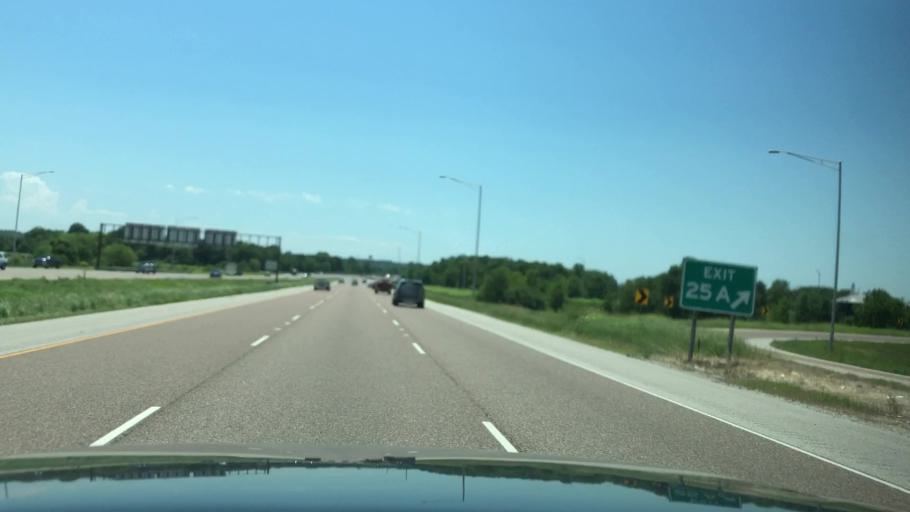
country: US
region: Illinois
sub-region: Saint Clair County
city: Caseyville
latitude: 38.6711
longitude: -90.0298
